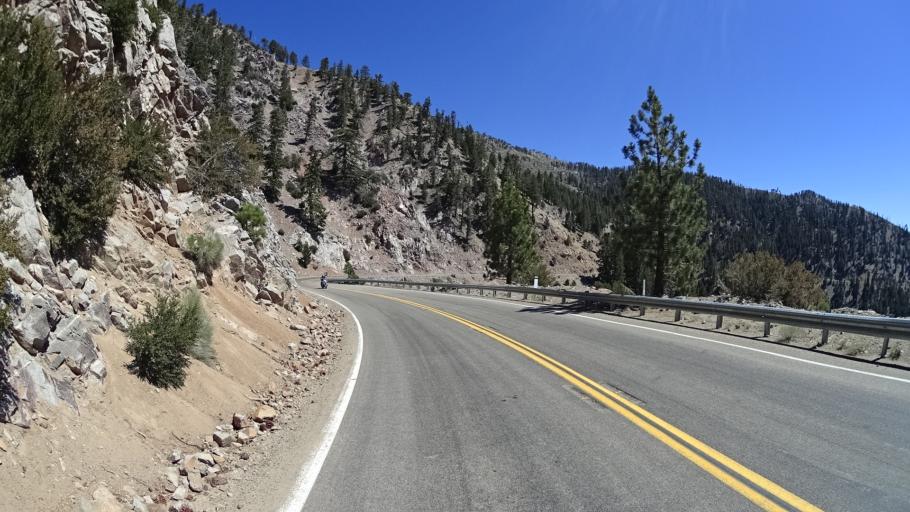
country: US
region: California
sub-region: San Bernardino County
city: Wrightwood
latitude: 34.3550
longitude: -117.8092
